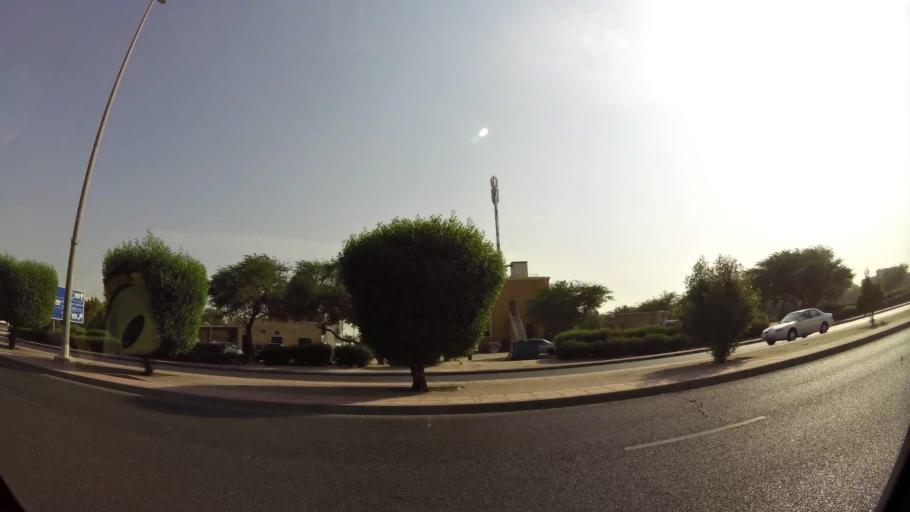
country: KW
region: Al Ahmadi
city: Ar Riqqah
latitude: 29.1572
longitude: 48.0885
